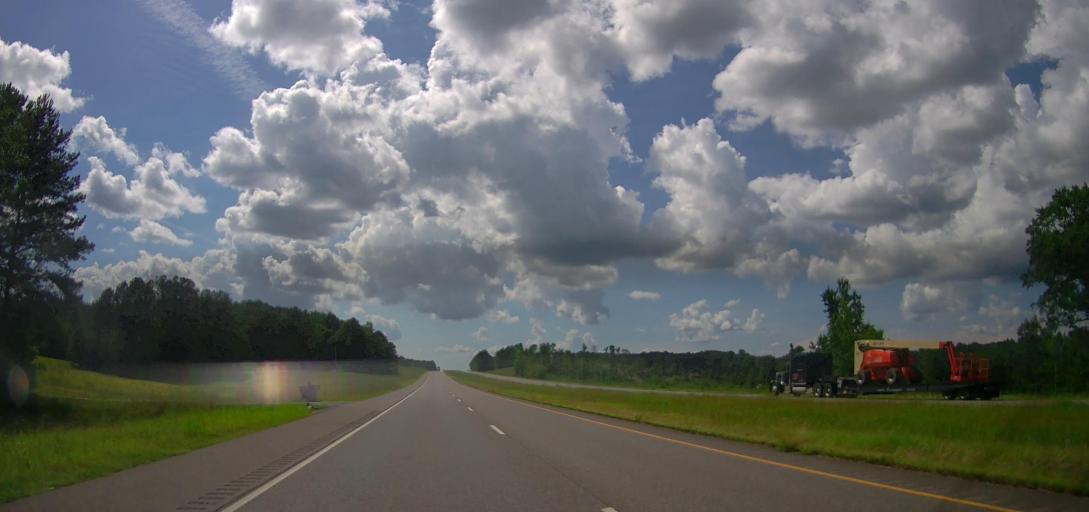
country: US
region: Alabama
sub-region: Pickens County
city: Reform
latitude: 33.3925
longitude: -88.0473
